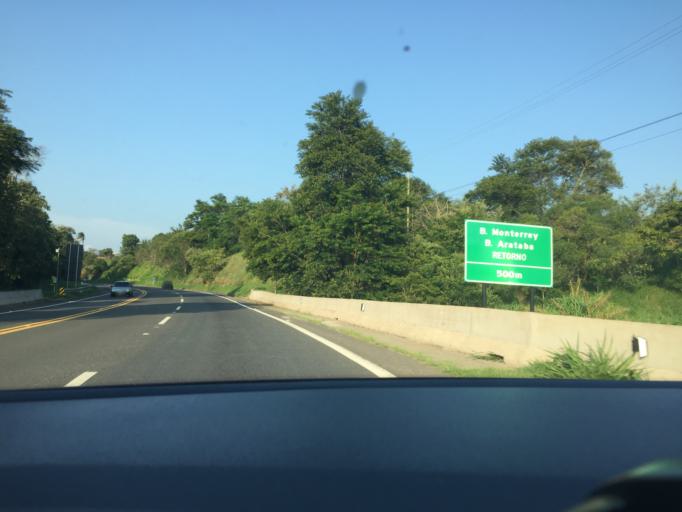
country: BR
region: Sao Paulo
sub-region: Louveira
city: Louveira
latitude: -23.0796
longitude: -46.9091
